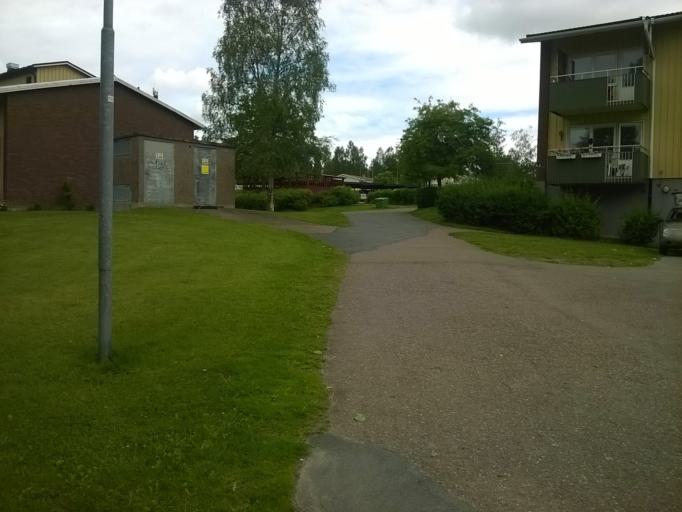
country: SE
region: Dalarna
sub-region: Saters Kommun
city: Saeter
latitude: 60.3413
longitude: 15.7497
